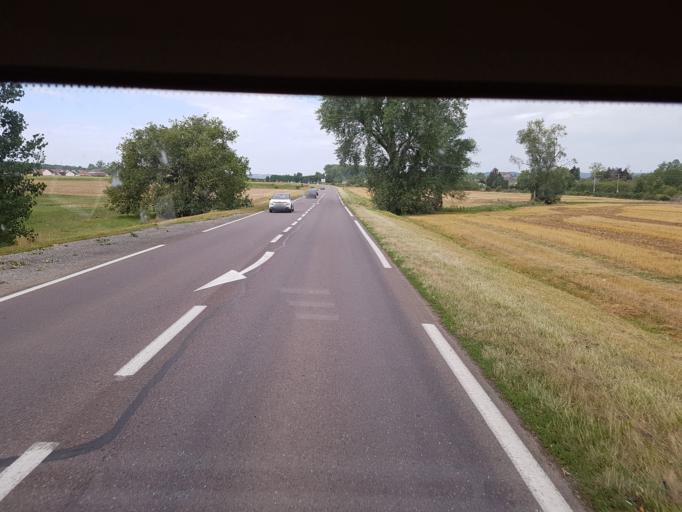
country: FR
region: Lorraine
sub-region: Departement de la Moselle
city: Basse-Ham
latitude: 49.3825
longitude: 6.2432
